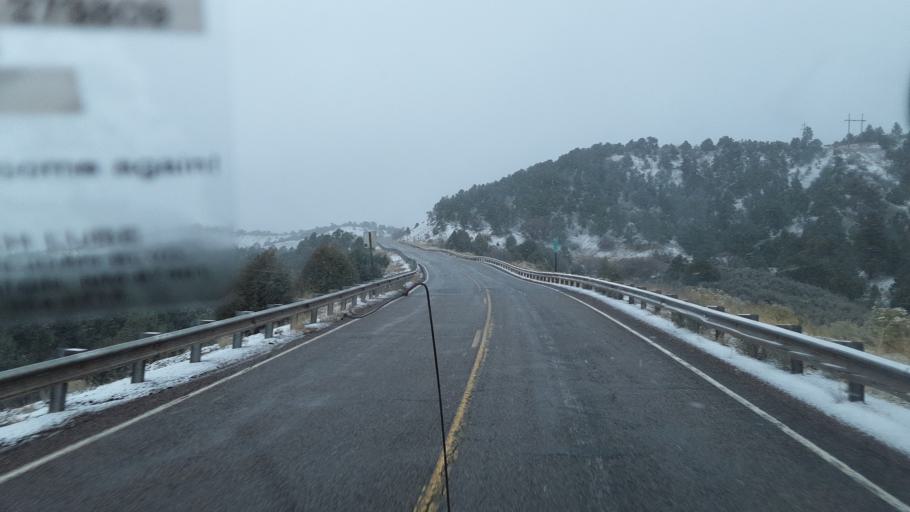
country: US
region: New Mexico
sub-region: Rio Arriba County
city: Tierra Amarilla
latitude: 36.6597
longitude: -106.5569
